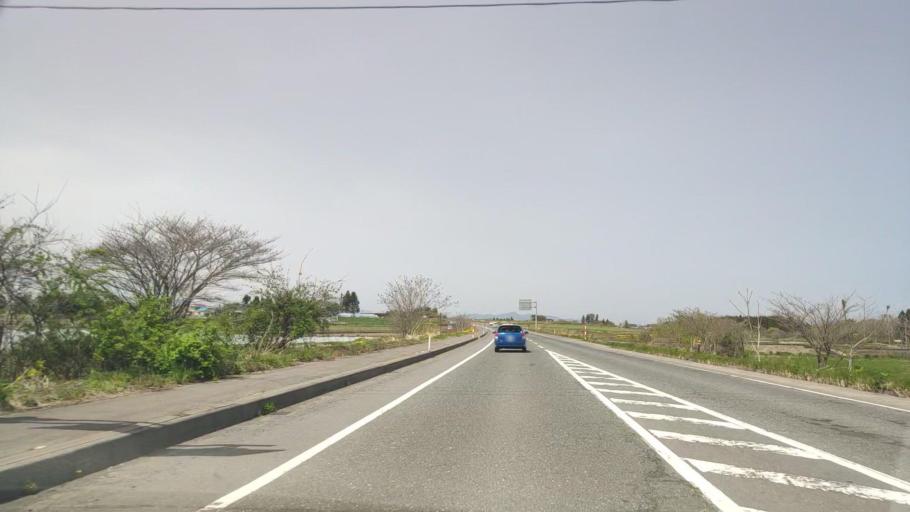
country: JP
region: Aomori
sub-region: Misawa Shi
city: Inuotose
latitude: 40.6342
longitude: 141.2448
